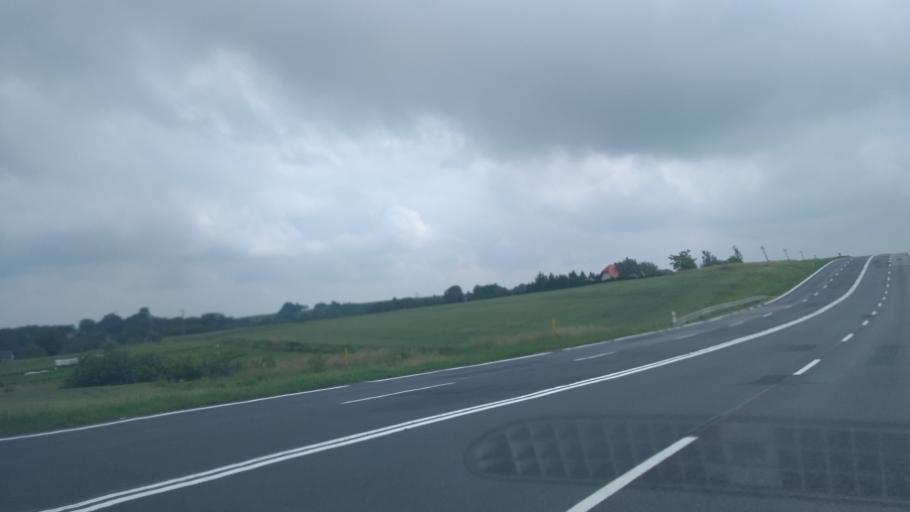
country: PL
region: Subcarpathian Voivodeship
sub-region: Powiat przeworski
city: Rozborz
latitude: 50.0477
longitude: 22.5365
